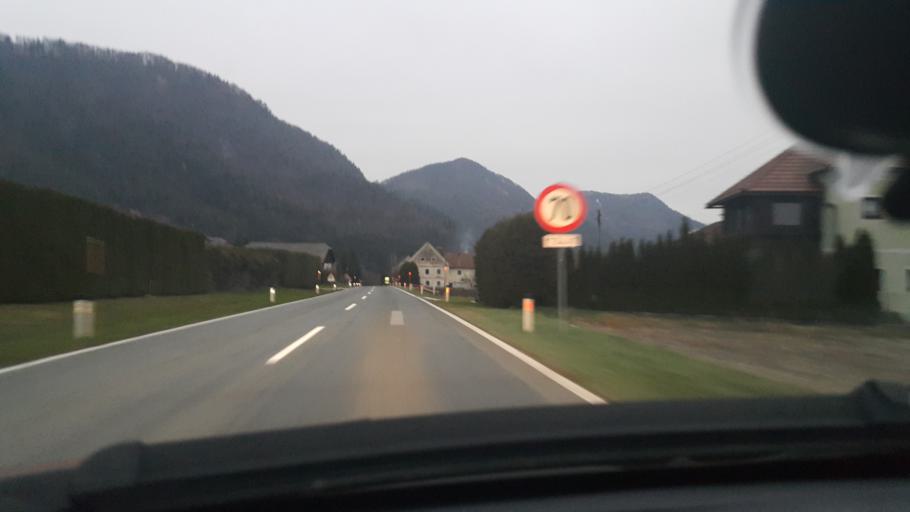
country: AT
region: Carinthia
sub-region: Politischer Bezirk Volkermarkt
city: Ruden
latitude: 46.6626
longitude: 14.8277
